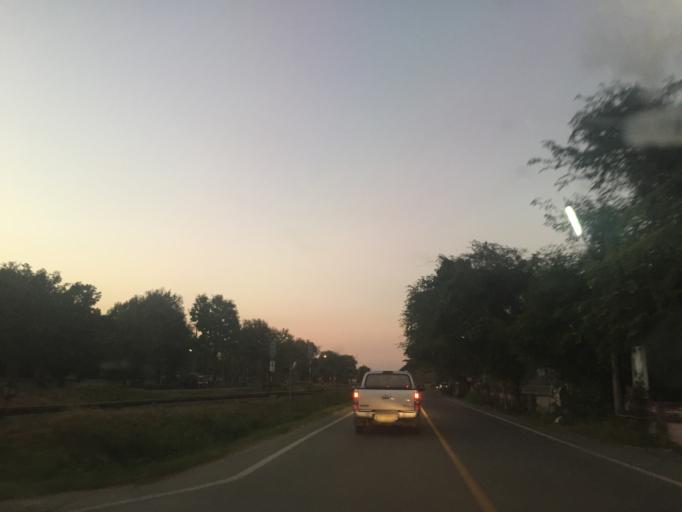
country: TH
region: Chiang Mai
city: Saraphi
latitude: 18.7077
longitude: 99.0430
